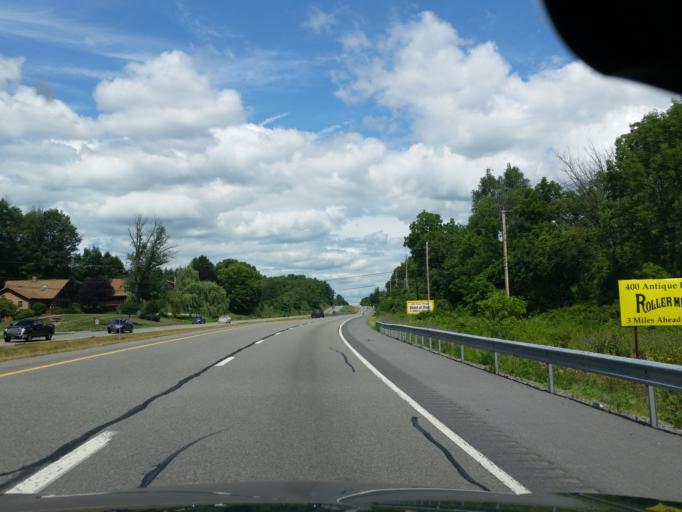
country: US
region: Pennsylvania
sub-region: Union County
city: Lewisburg
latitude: 40.9272
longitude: -76.8661
